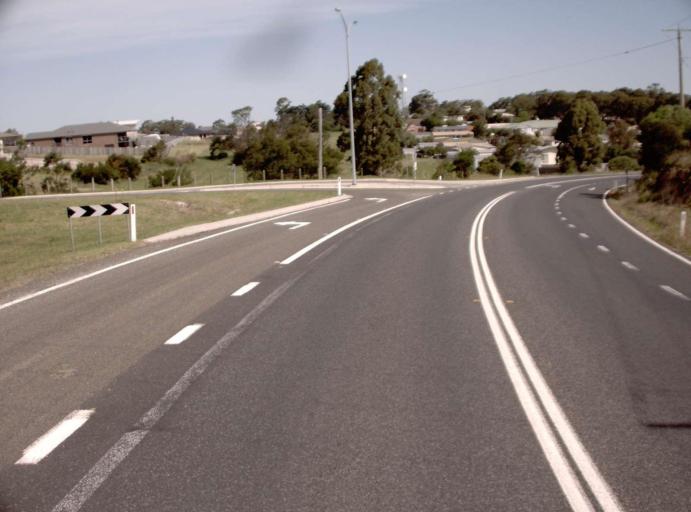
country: AU
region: Victoria
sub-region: East Gippsland
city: Lakes Entrance
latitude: -37.8736
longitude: 147.9612
